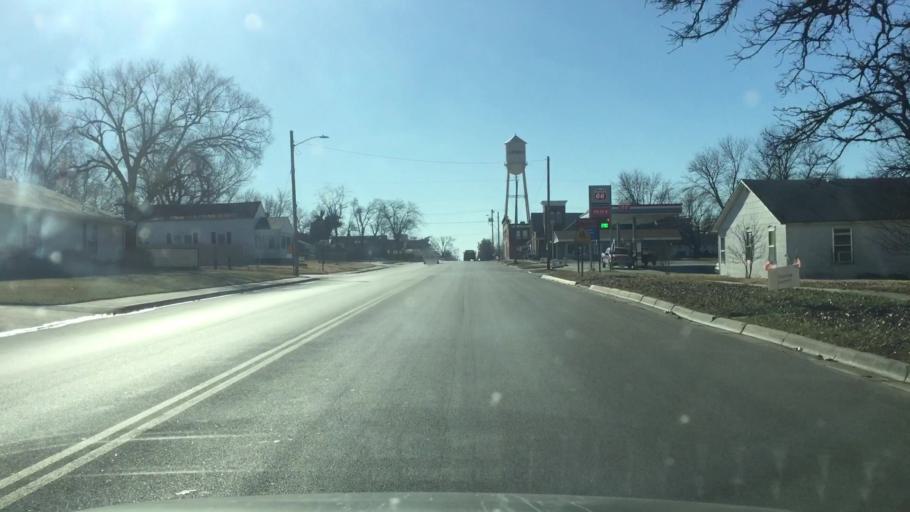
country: US
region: Kansas
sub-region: Allen County
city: Humboldt
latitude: 37.8136
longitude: -95.4356
